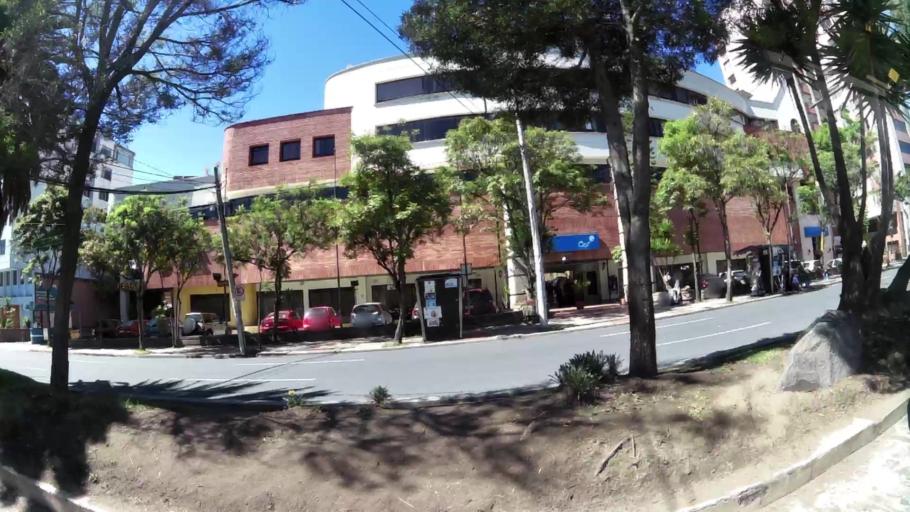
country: EC
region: Pichincha
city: Quito
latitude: -0.1945
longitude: -78.4932
